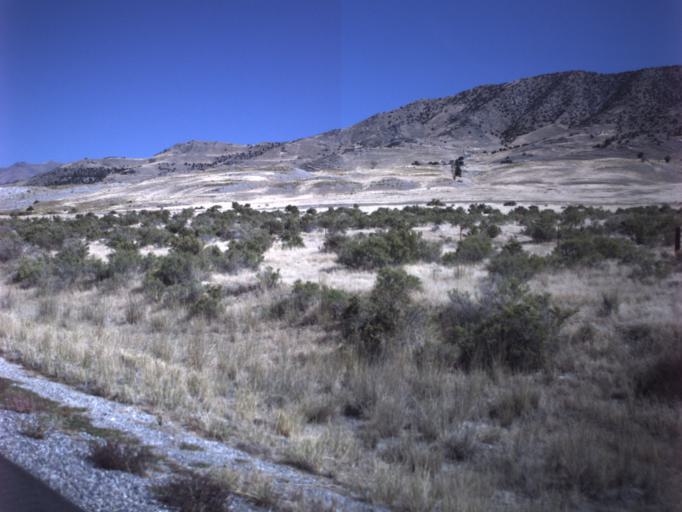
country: US
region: Utah
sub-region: Tooele County
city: Grantsville
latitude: 40.5534
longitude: -112.7390
